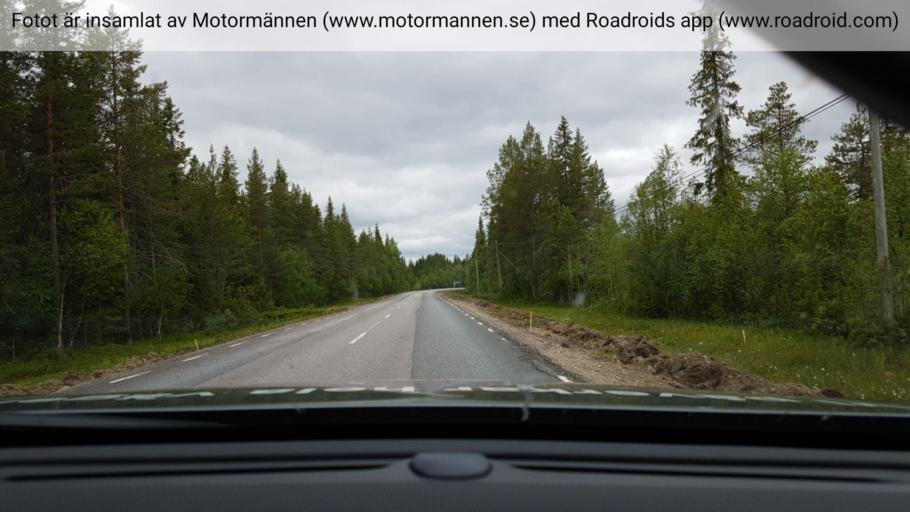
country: SE
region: Vaesterbotten
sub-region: Sorsele Kommun
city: Sorsele
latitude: 65.7720
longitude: 17.0284
